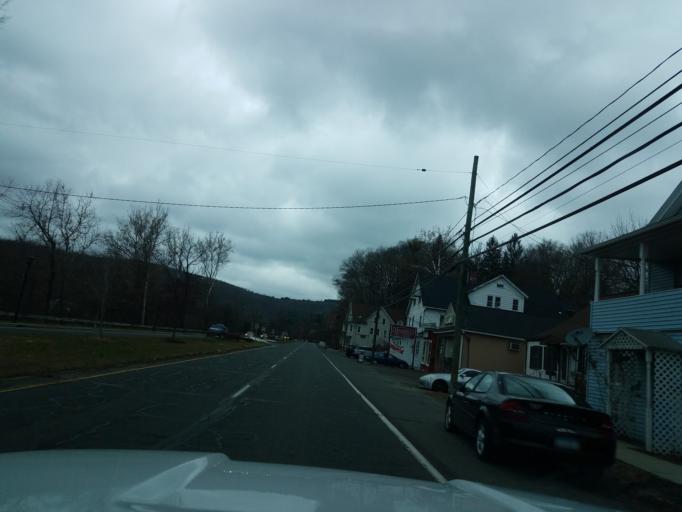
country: US
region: Connecticut
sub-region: New Haven County
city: Seymour
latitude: 41.4393
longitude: -73.0602
